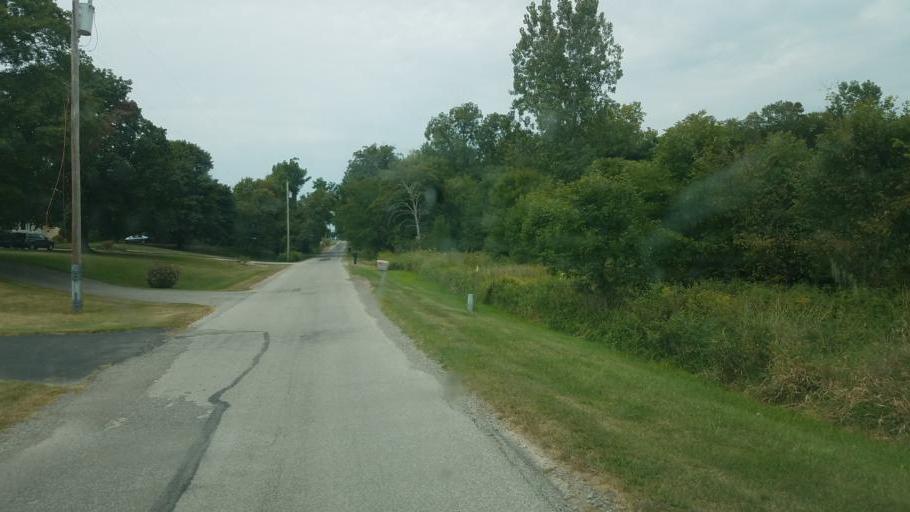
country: US
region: Ohio
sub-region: Marion County
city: Marion
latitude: 40.5132
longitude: -83.0994
